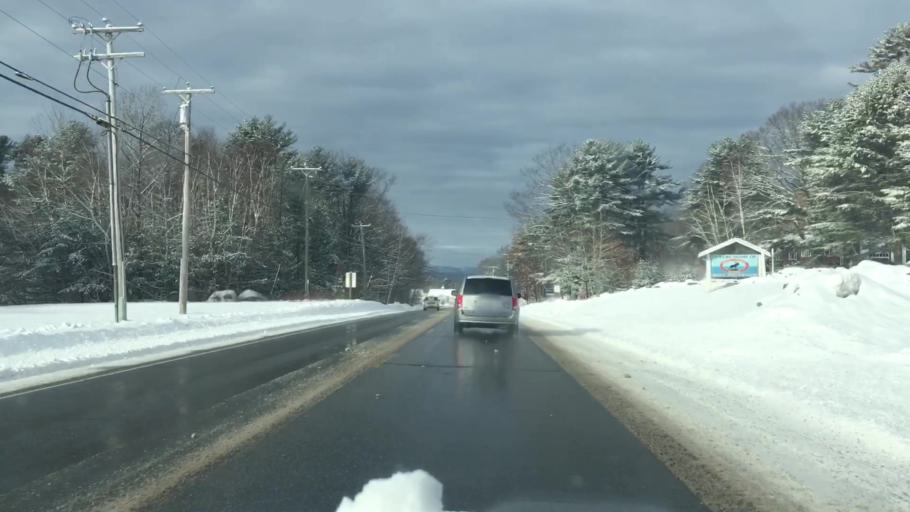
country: US
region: Maine
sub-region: Cumberland County
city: Raymond
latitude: 43.9677
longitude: -70.5856
